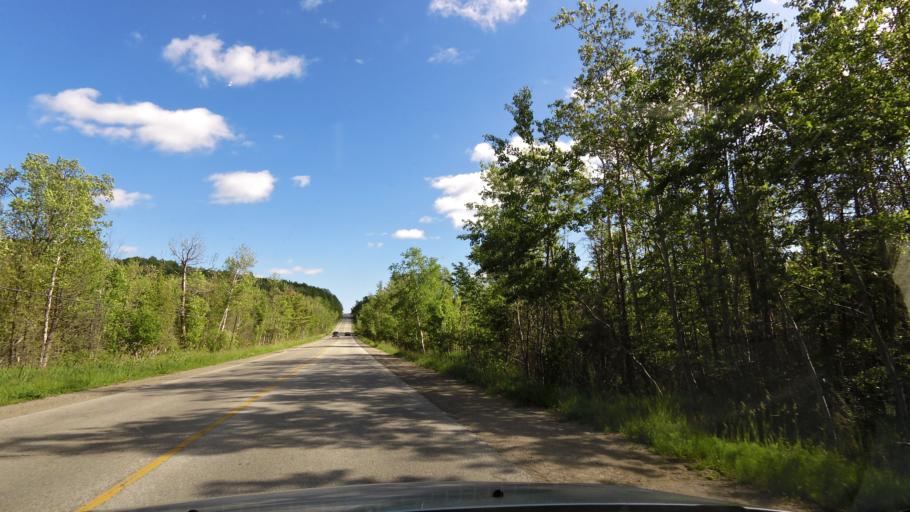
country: CA
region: Ontario
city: Bradford West Gwillimbury
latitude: 44.1717
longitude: -79.6181
